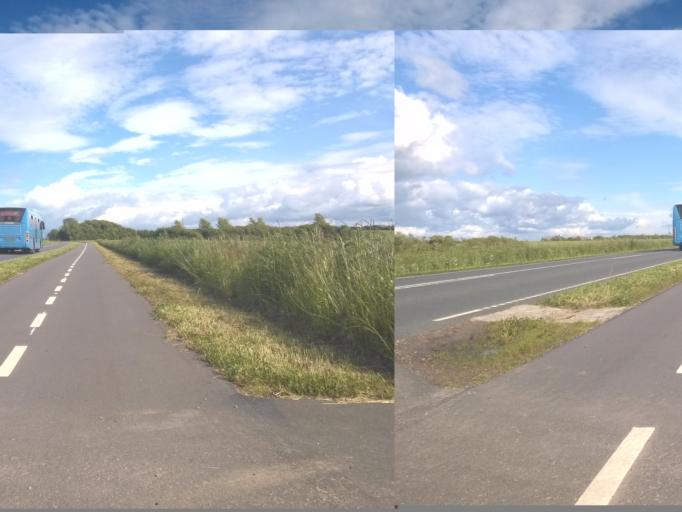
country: DK
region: Central Jutland
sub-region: Holstebro Kommune
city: Vinderup
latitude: 56.4662
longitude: 8.8409
